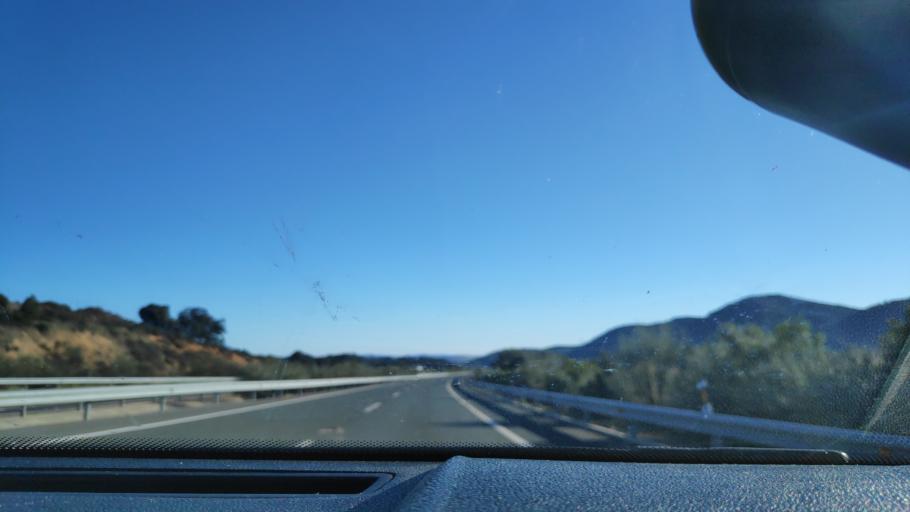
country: ES
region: Extremadura
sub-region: Provincia de Badajoz
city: Monesterio
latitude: 38.0650
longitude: -6.2436
